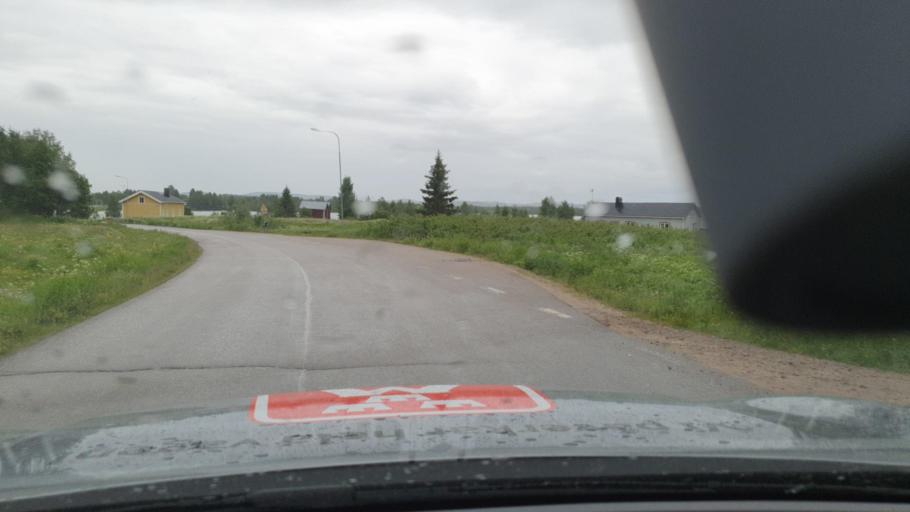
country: SE
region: Norrbotten
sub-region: Pajala Kommun
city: Pajala
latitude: 66.8055
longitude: 23.1188
